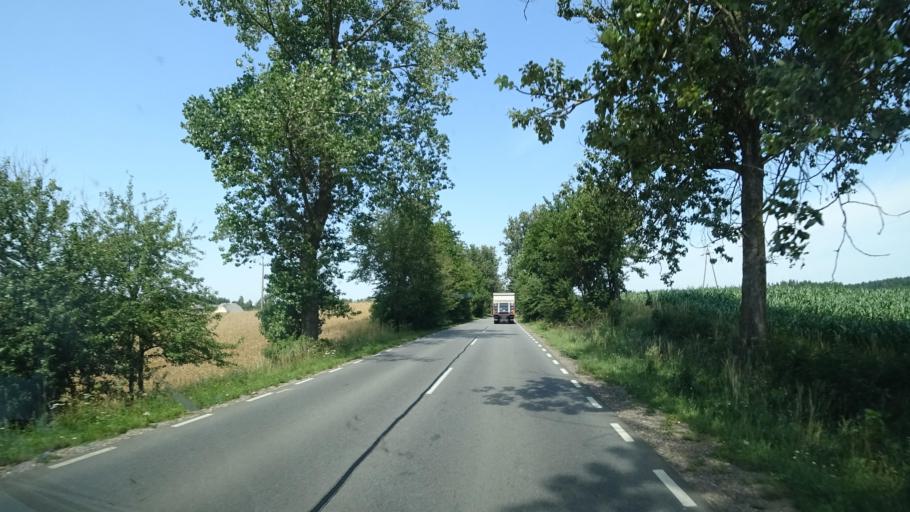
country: PL
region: Pomeranian Voivodeship
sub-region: Powiat koscierski
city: Lipusz
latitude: 54.0816
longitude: 17.7974
